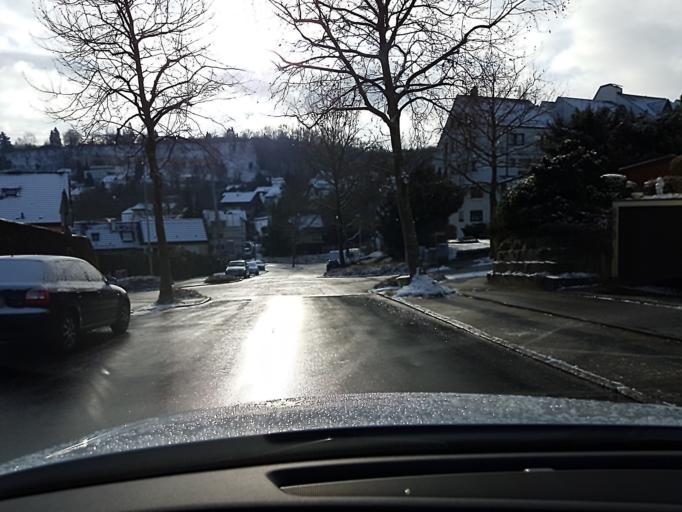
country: DE
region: Baden-Wuerttemberg
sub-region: Regierungsbezirk Stuttgart
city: Weinsberg
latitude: 49.1465
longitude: 9.2790
